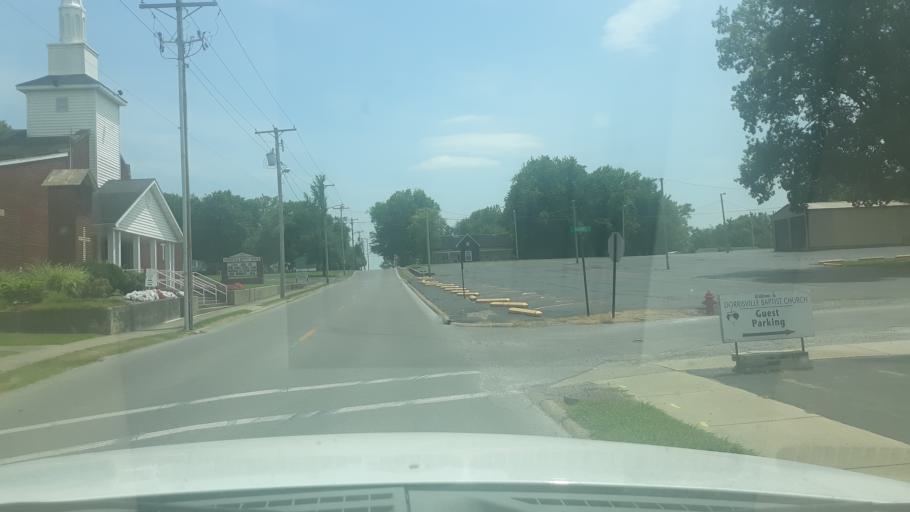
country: US
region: Illinois
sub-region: Saline County
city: Harrisburg
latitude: 37.7230
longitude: -88.5531
